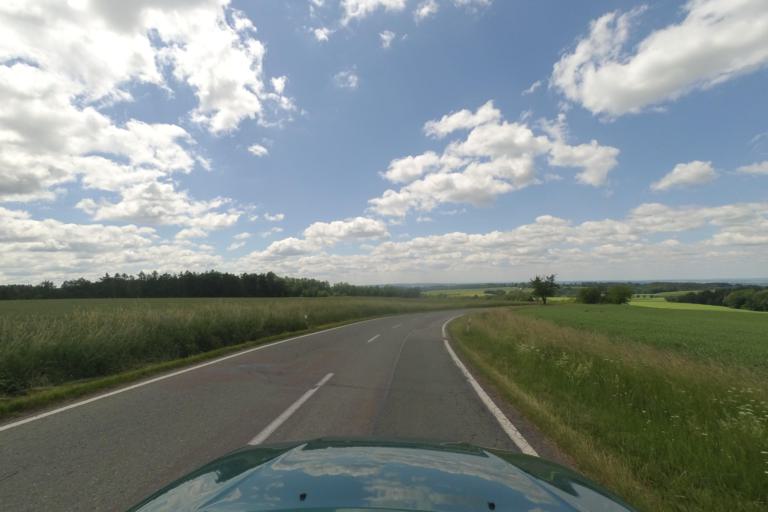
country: CZ
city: Nove Mesto nad Metuji
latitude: 50.3331
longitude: 16.2225
